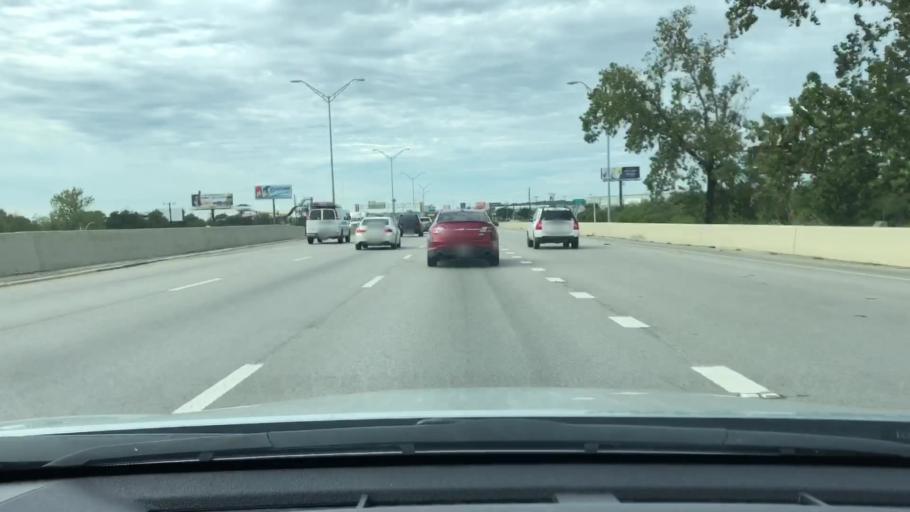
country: US
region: Texas
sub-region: Bexar County
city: Terrell Hills
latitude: 29.4509
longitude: -98.4215
